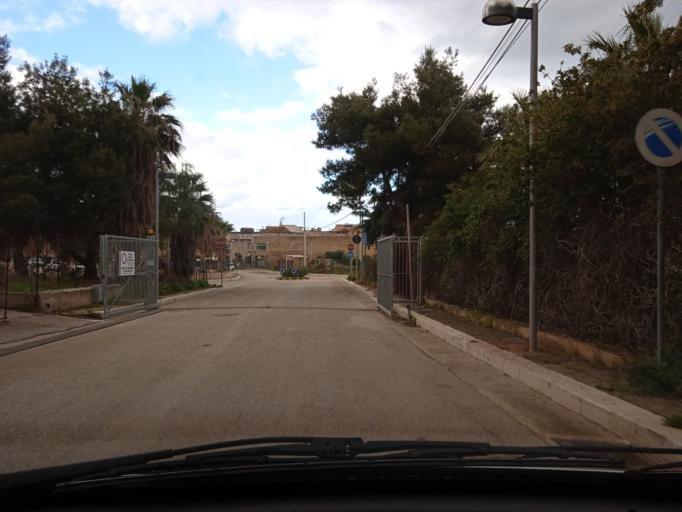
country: IT
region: Sicily
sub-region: Palermo
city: Villabate
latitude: 38.0734
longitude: 13.4413
